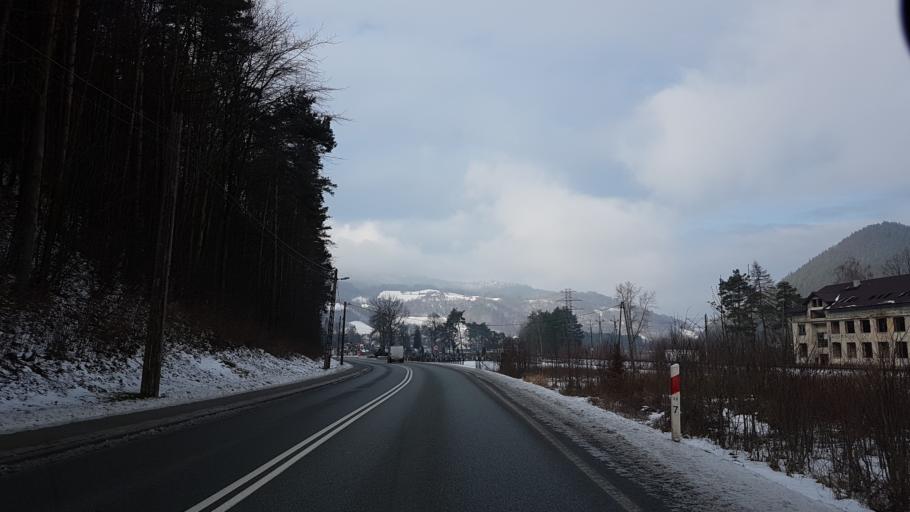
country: PL
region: Lesser Poland Voivodeship
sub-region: Powiat nowosadecki
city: Piwniczna-Zdroj
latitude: 49.4463
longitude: 20.7091
